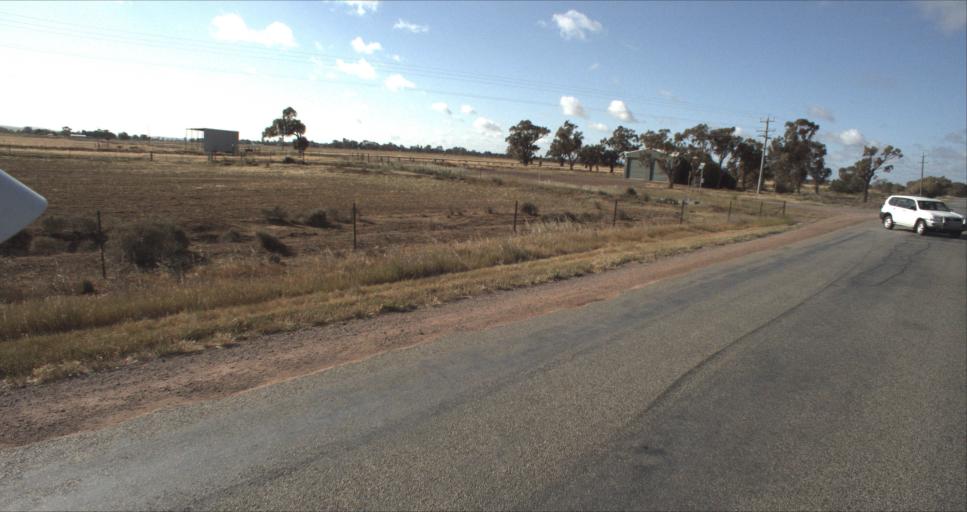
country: AU
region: New South Wales
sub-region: Leeton
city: Leeton
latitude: -34.5106
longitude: 146.3923
